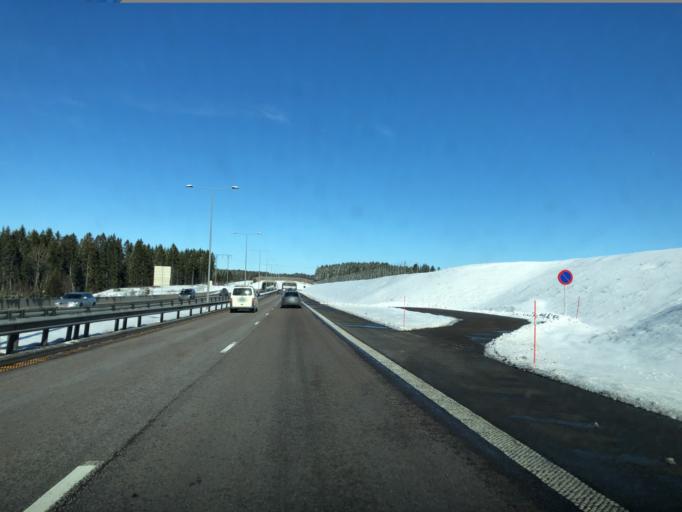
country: NO
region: Vestfold
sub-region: Sandefjord
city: Sandefjord
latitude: 59.1841
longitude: 10.2079
